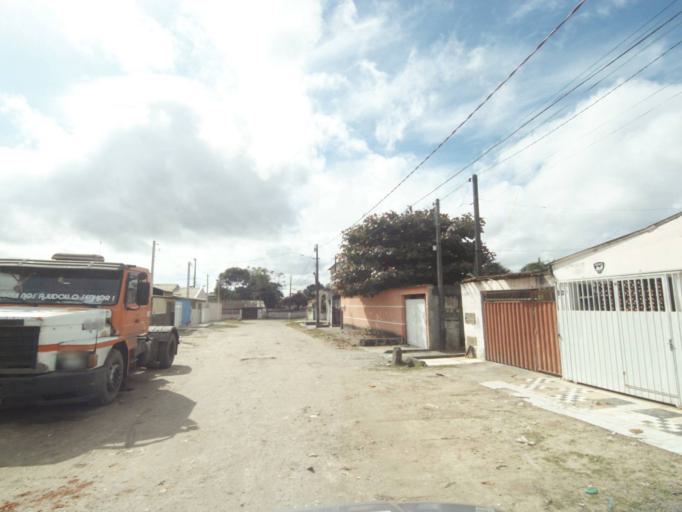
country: BR
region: Parana
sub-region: Paranagua
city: Paranagua
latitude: -25.5709
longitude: -48.5620
